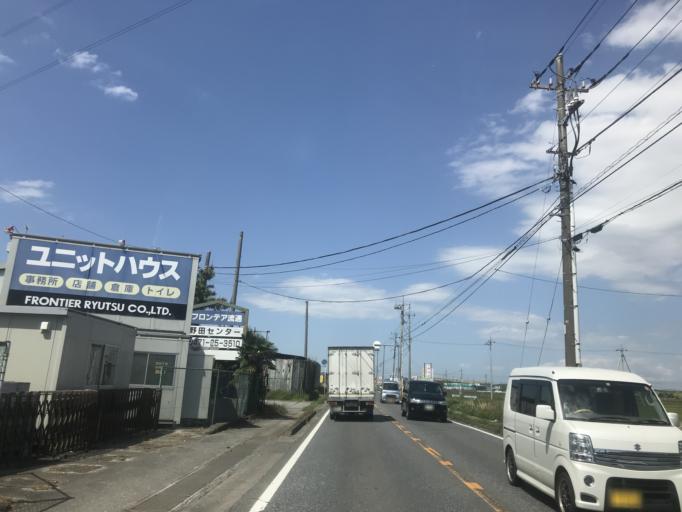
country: JP
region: Chiba
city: Noda
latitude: 35.9735
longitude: 139.8851
